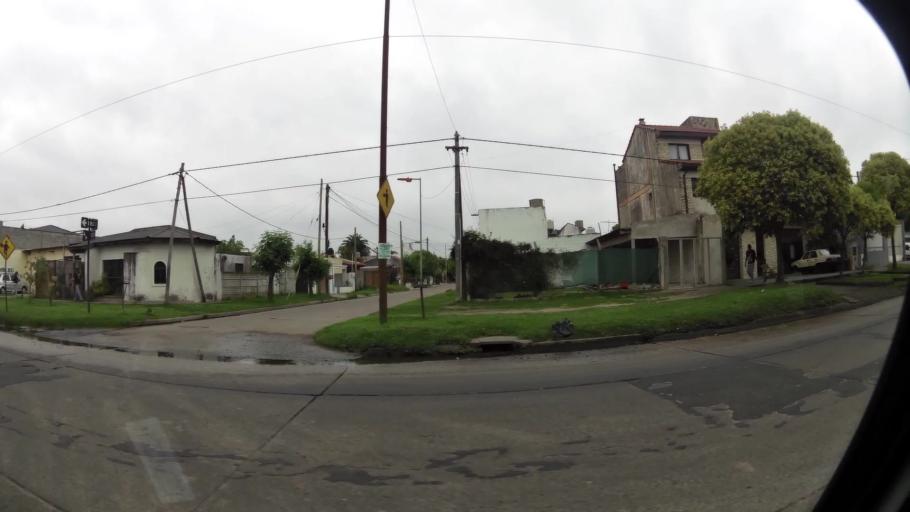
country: AR
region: Buenos Aires
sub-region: Partido de La Plata
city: La Plata
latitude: -34.8812
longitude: -57.9675
